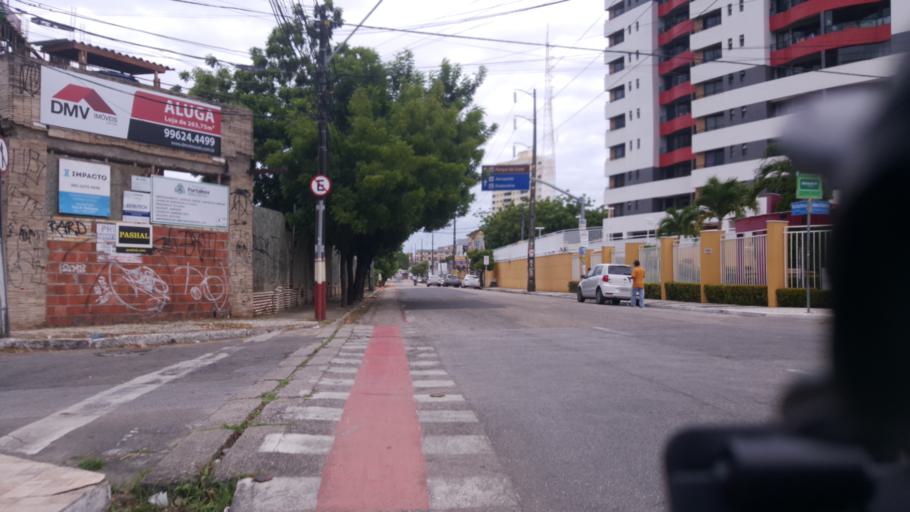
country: BR
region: Ceara
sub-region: Fortaleza
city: Fortaleza
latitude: -3.7461
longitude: -38.5126
